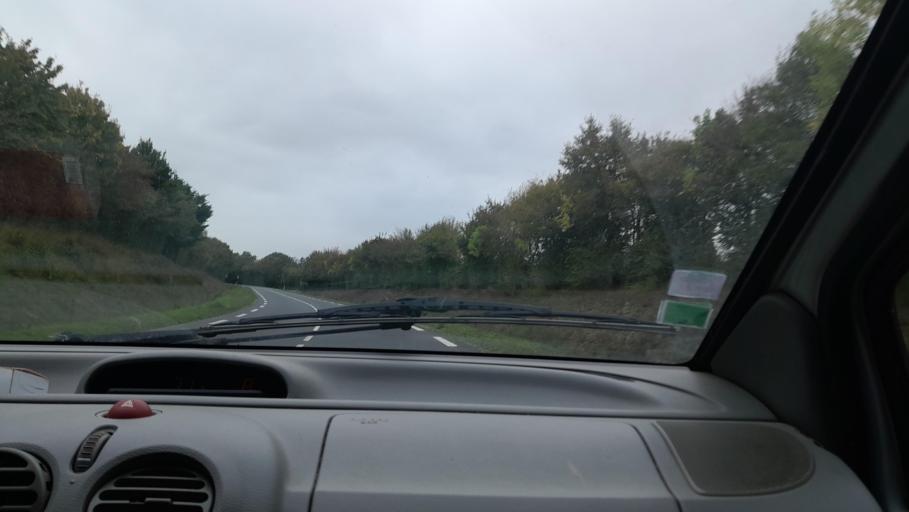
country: FR
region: Pays de la Loire
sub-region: Departement de la Loire-Atlantique
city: Saint-Mars-la-Jaille
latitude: 47.5286
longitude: -1.1794
